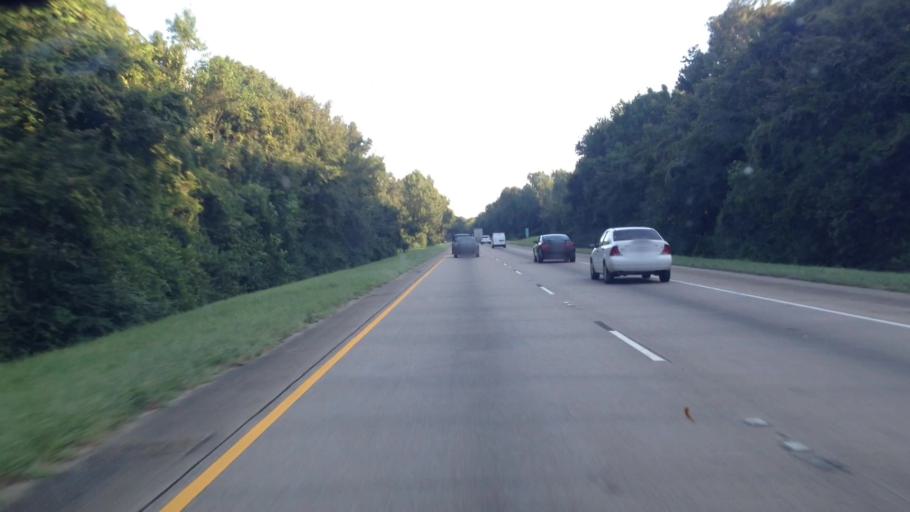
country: US
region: Louisiana
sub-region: Ascension Parish
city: Prairieville
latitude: 30.2978
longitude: -90.9917
